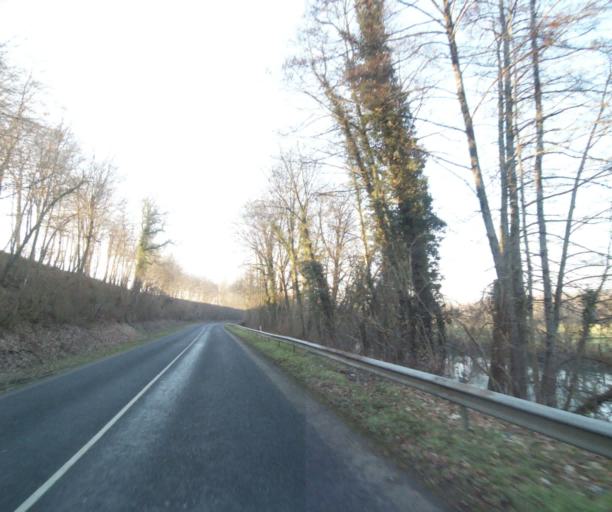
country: FR
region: Champagne-Ardenne
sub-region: Departement de la Haute-Marne
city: Bienville
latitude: 48.5583
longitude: 5.0605
